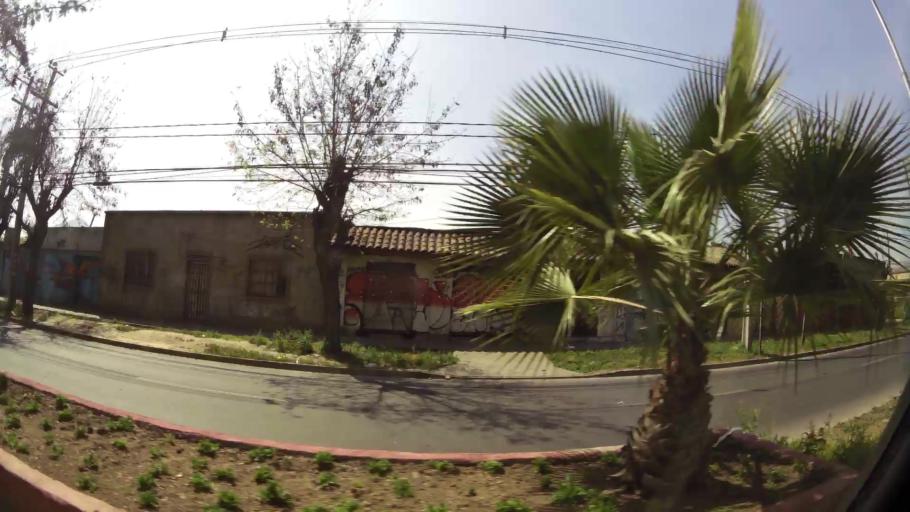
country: CL
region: Santiago Metropolitan
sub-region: Provincia de Santiago
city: Lo Prado
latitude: -33.4187
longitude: -70.7072
